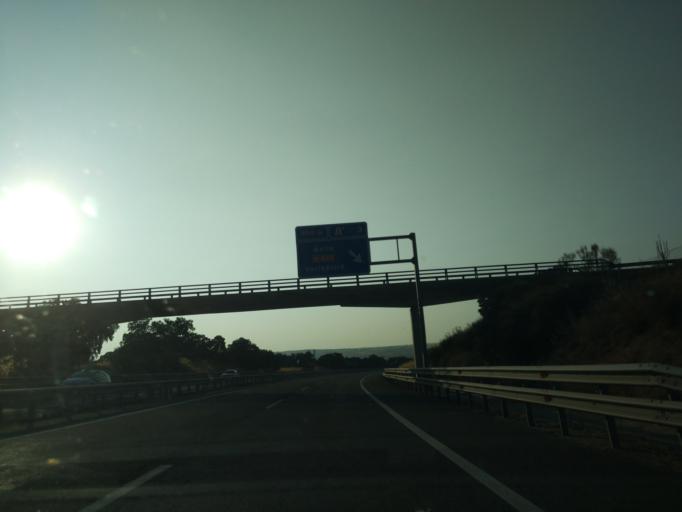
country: ES
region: Castille and Leon
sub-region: Provincia de Avila
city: Avila
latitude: 40.6714
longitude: -4.6756
